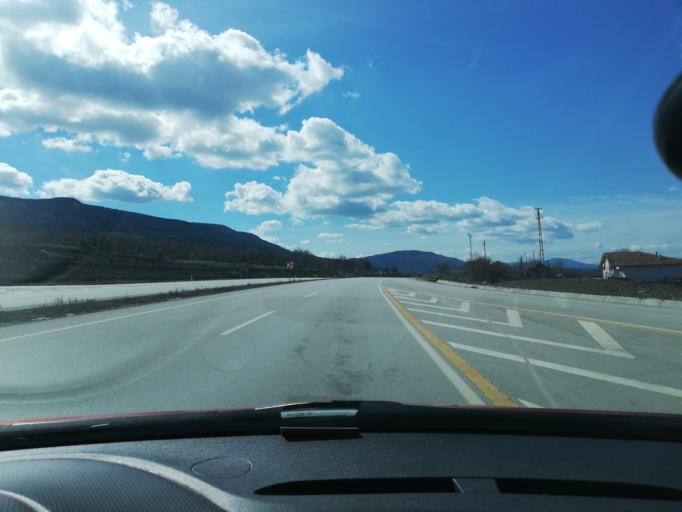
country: TR
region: Kastamonu
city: Igdir
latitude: 41.2209
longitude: 32.9930
